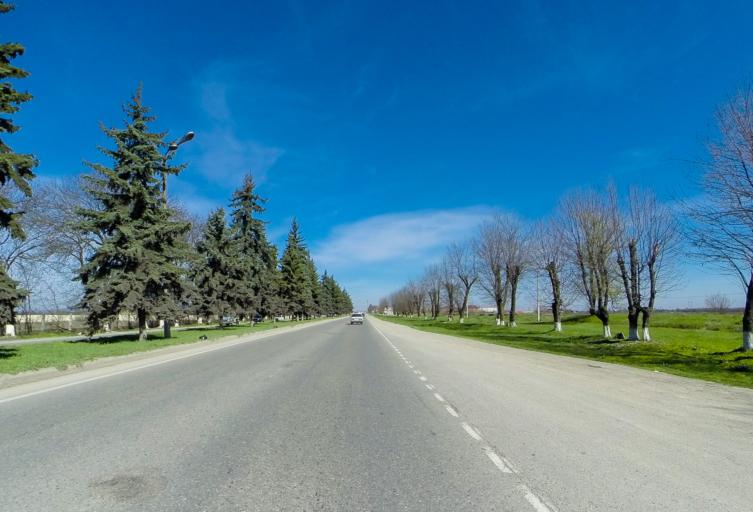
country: RU
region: Kabardino-Balkariya
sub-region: Gorod Nal'chik
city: Nal'chik
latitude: 43.5281
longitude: 43.6084
